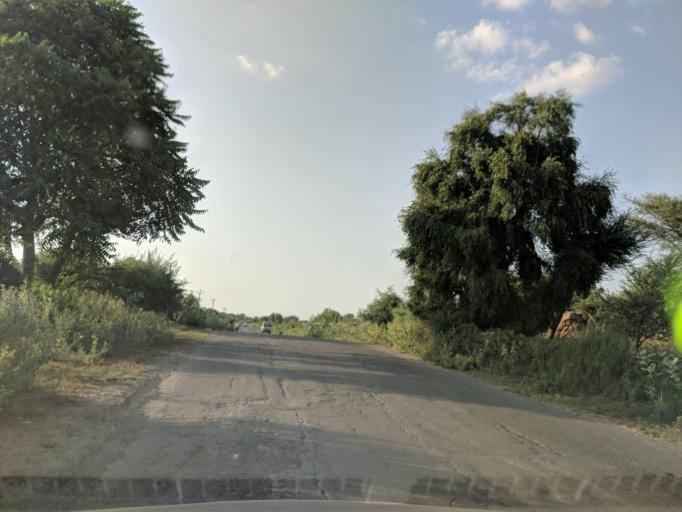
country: IN
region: Rajasthan
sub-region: Churu
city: Rajgarh
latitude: 28.5380
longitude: 75.3755
